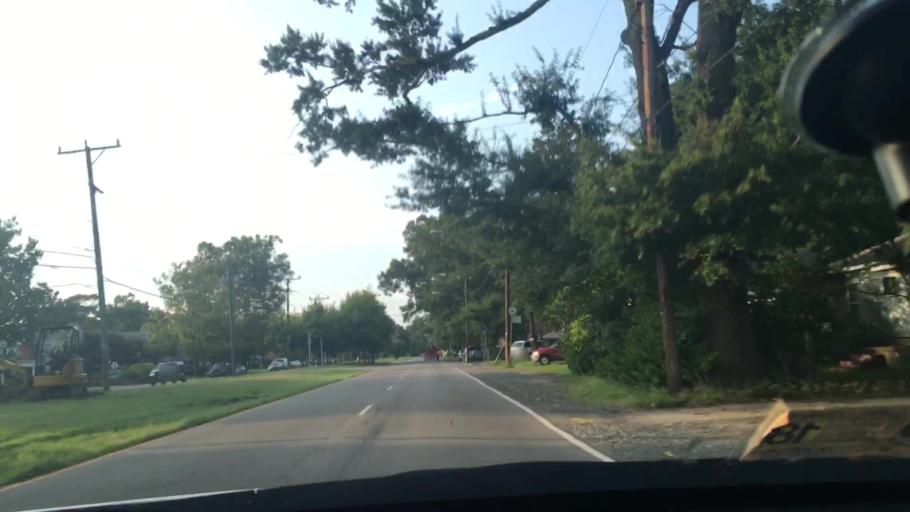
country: US
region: Virginia
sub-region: City of Norfolk
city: Norfolk
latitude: 36.9387
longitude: -76.2450
